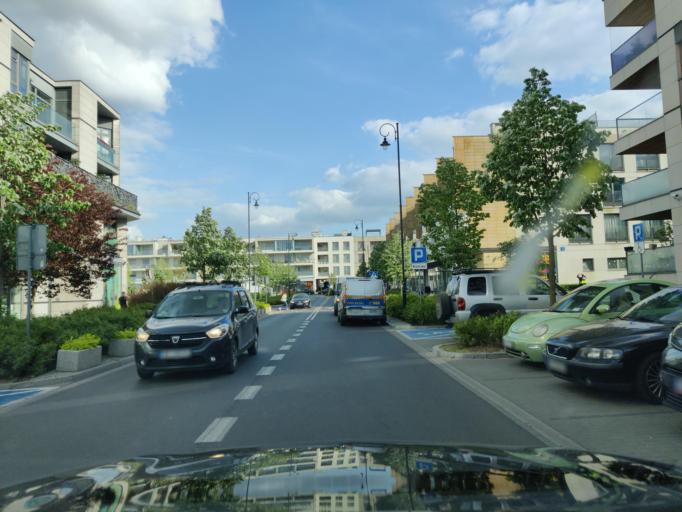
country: PL
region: Masovian Voivodeship
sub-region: Warszawa
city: Wilanow
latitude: 52.1625
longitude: 21.0799
